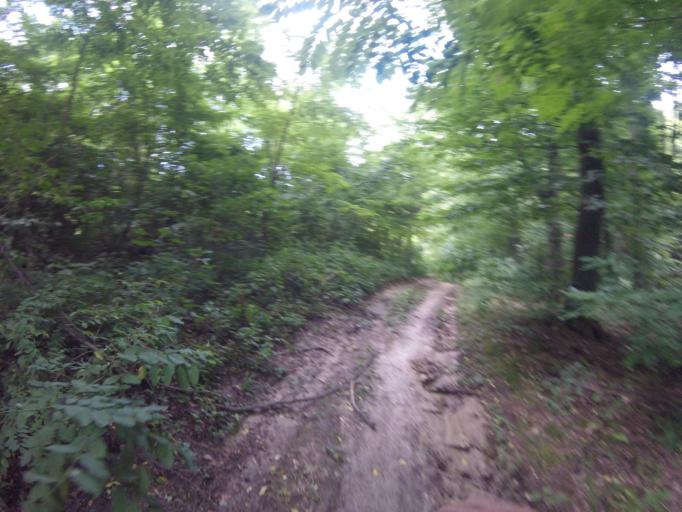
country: HU
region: Zala
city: Nagykanizsa
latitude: 46.5594
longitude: 17.0360
